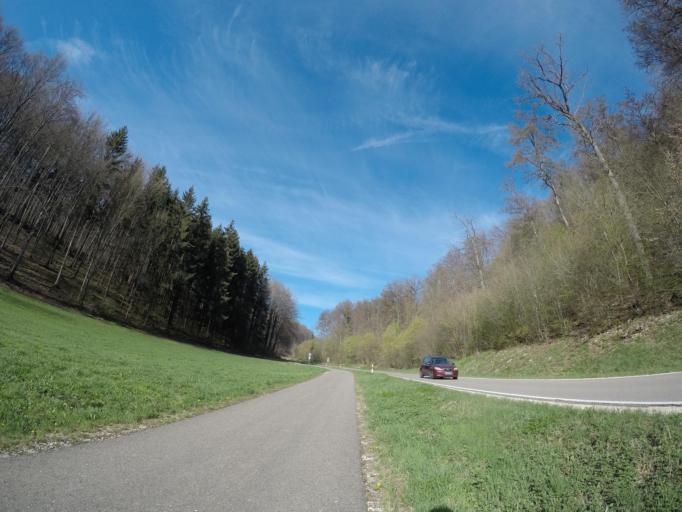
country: DE
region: Baden-Wuerttemberg
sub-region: Tuebingen Region
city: Allmendingen
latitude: 48.3476
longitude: 9.6786
